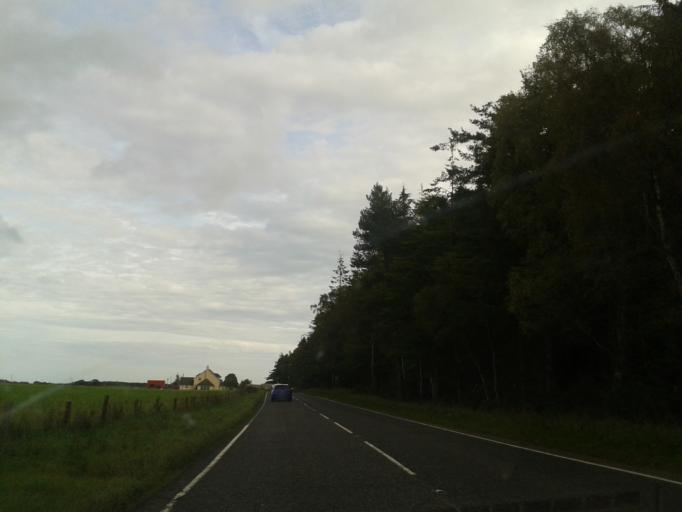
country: GB
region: Scotland
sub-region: Moray
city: Fochabers
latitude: 57.6293
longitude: -3.0421
